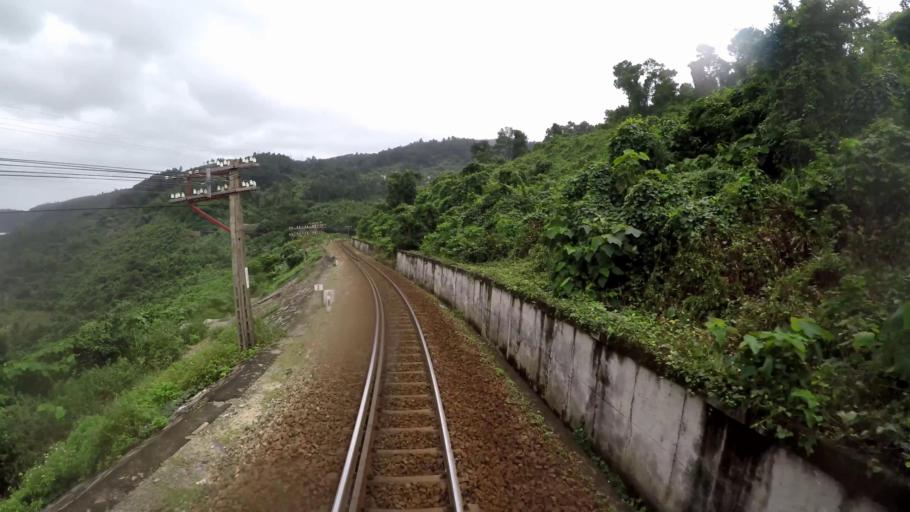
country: VN
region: Da Nang
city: Lien Chieu
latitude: 16.1636
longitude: 108.1338
